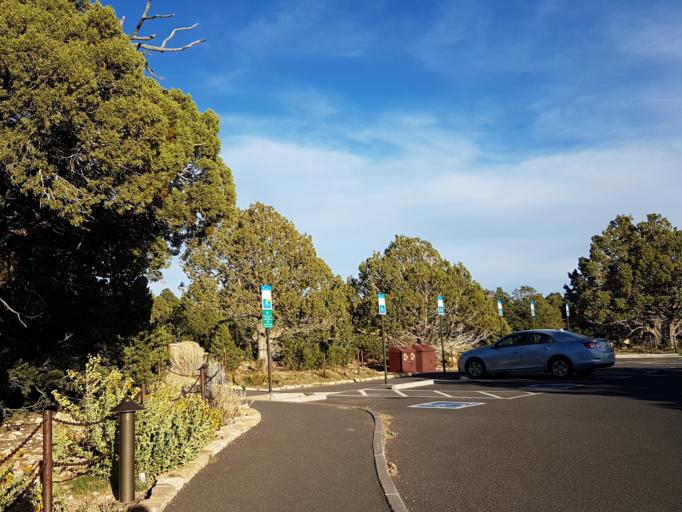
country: US
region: Arizona
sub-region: Coconino County
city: Grand Canyon
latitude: 36.0594
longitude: -112.1072
